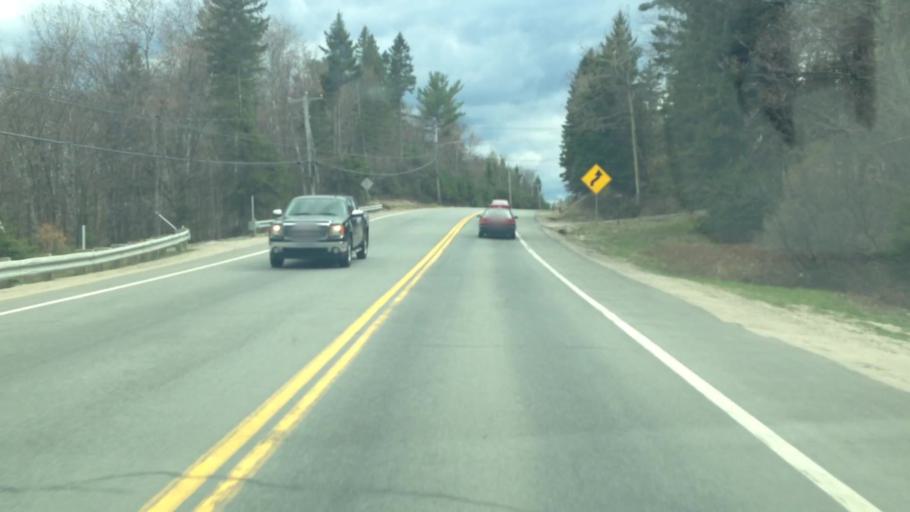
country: CA
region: Quebec
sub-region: Laurentides
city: Sainte-Adele
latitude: 45.9980
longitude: -74.1119
